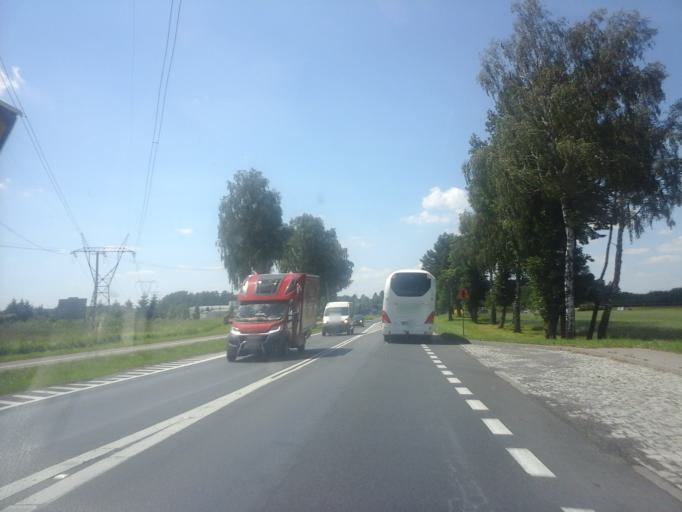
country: PL
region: West Pomeranian Voivodeship
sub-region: Koszalin
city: Koszalin
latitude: 54.1665
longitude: 16.0951
